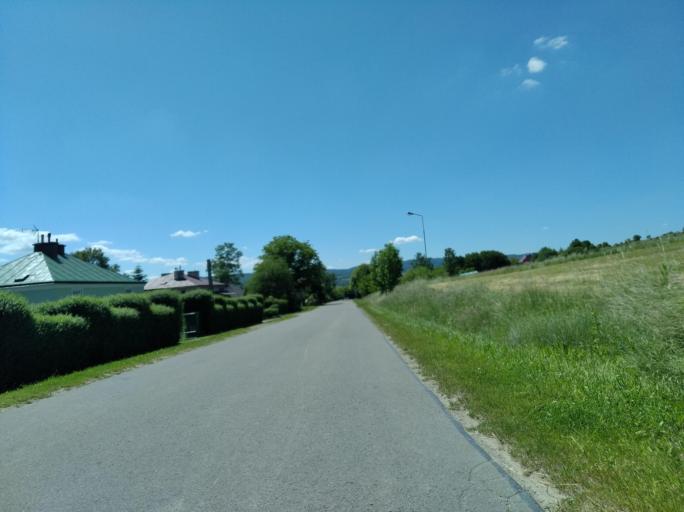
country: PL
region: Subcarpathian Voivodeship
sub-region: Powiat jasielski
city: Nowy Zmigrod
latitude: 49.6250
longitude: 21.5852
